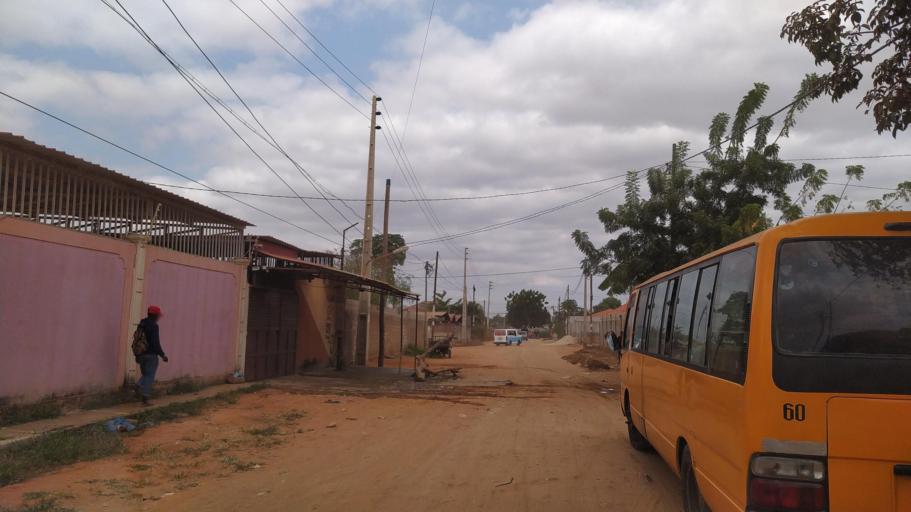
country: AO
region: Luanda
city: Luanda
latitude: -8.9277
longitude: 13.2614
